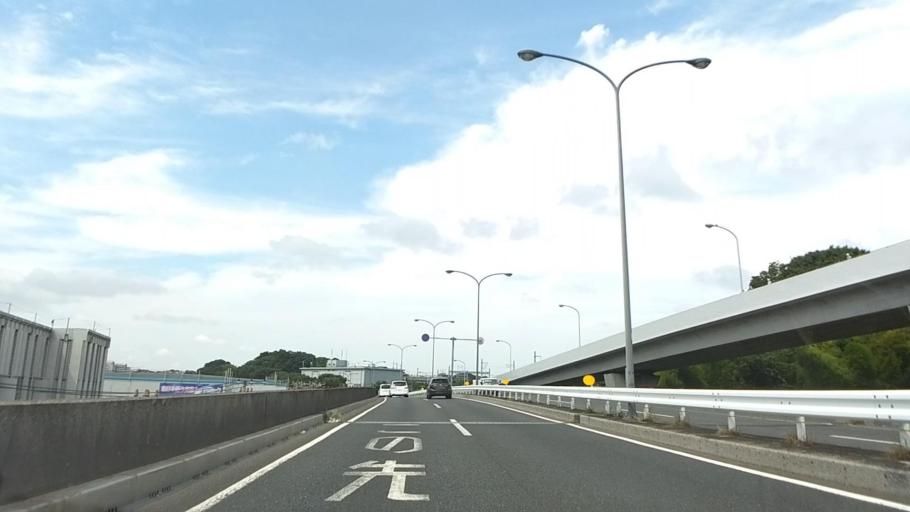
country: JP
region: Kanagawa
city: Yokohama
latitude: 35.4865
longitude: 139.5922
